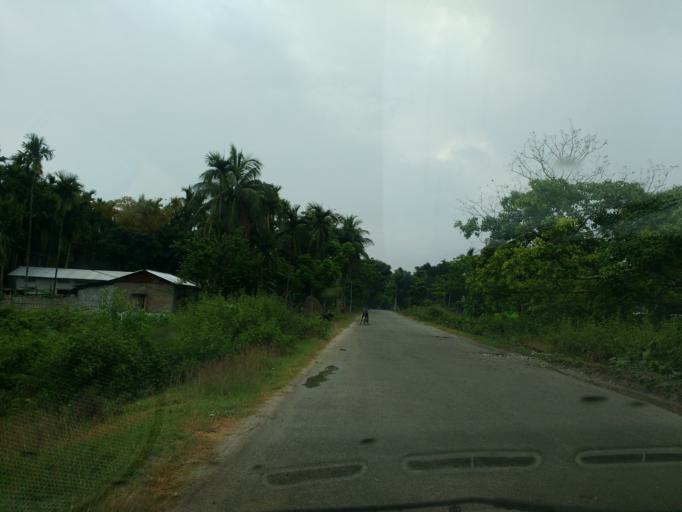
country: IN
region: Assam
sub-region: Udalguri
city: Udalguri
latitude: 26.7272
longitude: 92.2119
